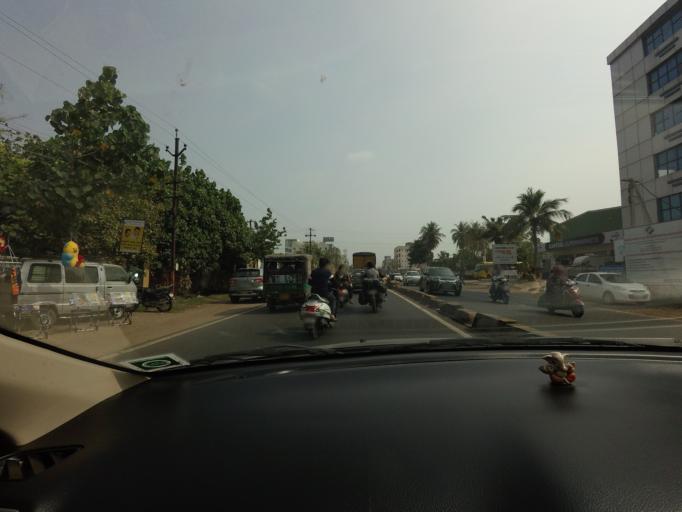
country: IN
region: Andhra Pradesh
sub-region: Krishna
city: Yanamalakuduru
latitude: 16.4883
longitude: 80.6760
